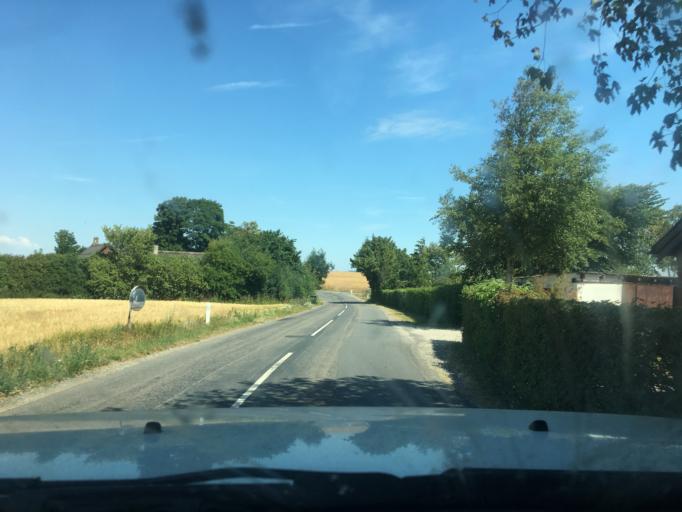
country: DK
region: Central Jutland
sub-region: Arhus Kommune
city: Trige
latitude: 56.3426
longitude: 10.2047
